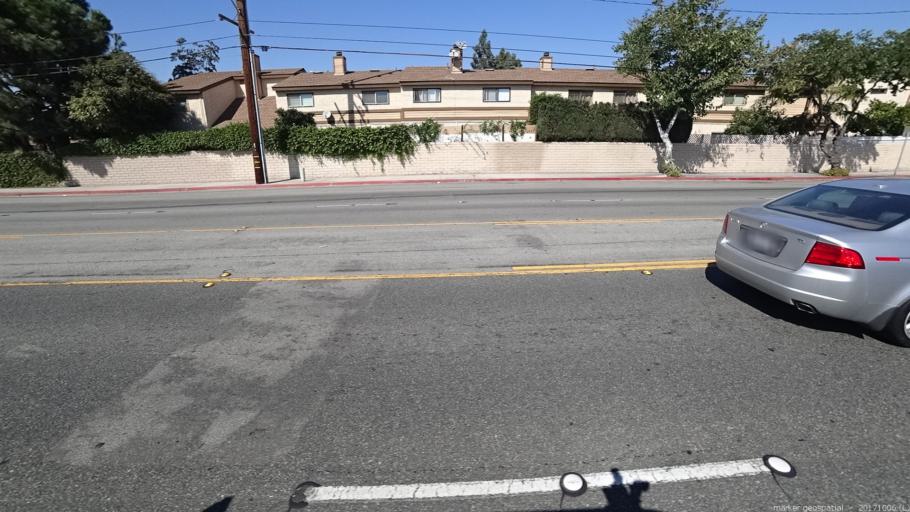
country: US
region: California
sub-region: Orange County
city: Stanton
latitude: 33.7884
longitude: -117.9852
